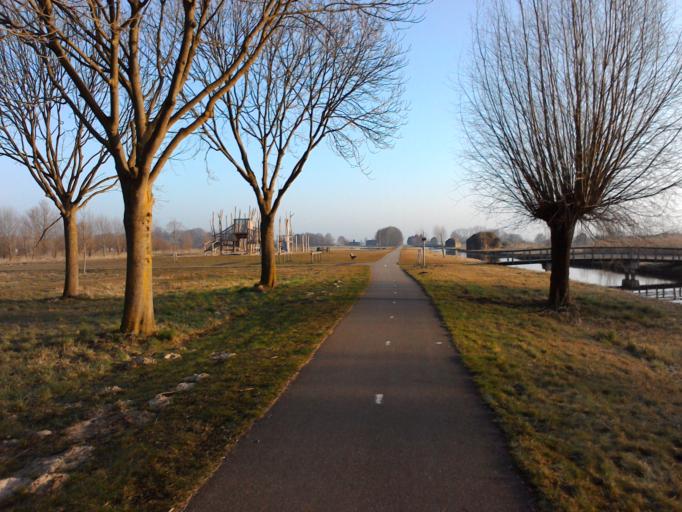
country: NL
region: Utrecht
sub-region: Gemeente Utrecht
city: Utrecht
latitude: 52.1212
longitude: 5.1303
